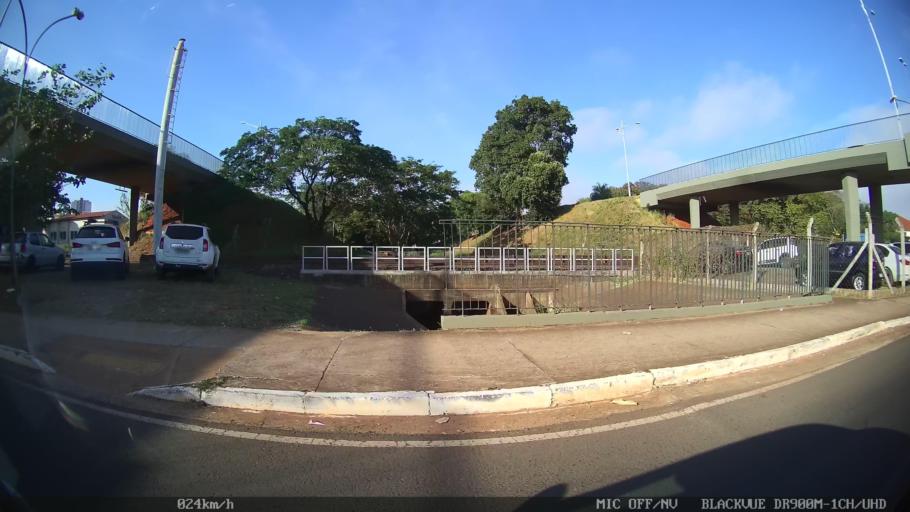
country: BR
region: Sao Paulo
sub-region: Sao Jose Do Rio Preto
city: Sao Jose do Rio Preto
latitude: -20.8112
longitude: -49.3678
